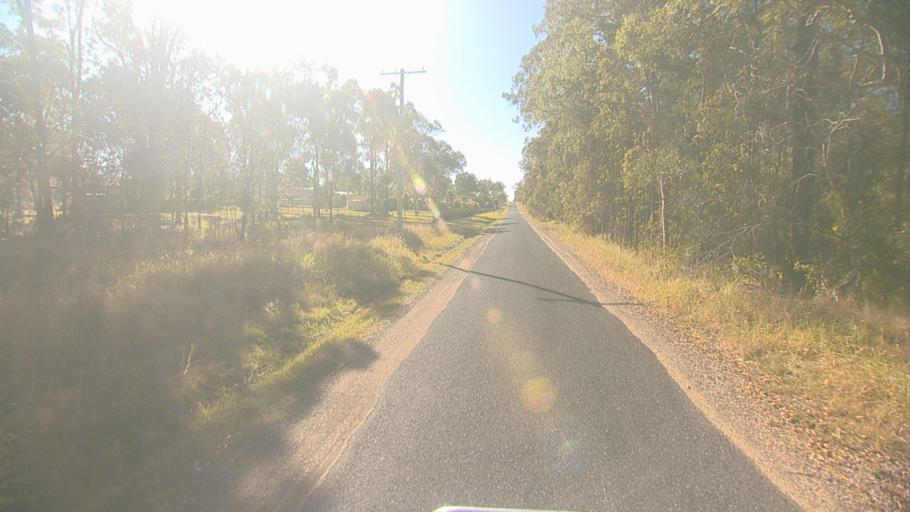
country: AU
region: Queensland
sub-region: Logan
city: Park Ridge South
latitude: -27.7469
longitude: 153.0359
